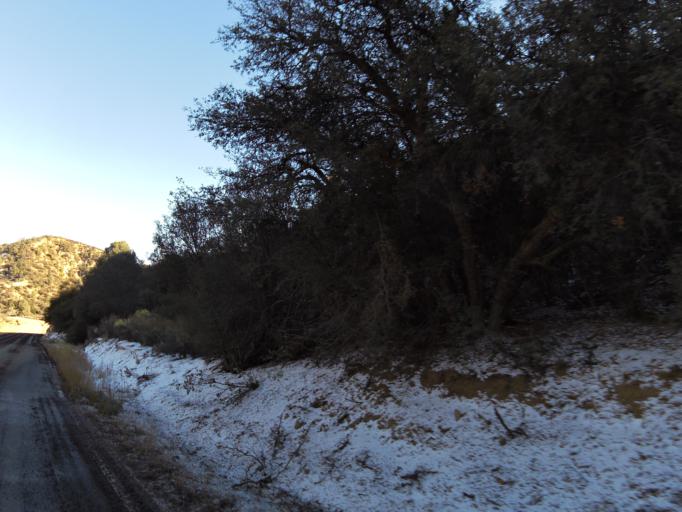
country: US
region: California
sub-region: Ventura County
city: Meiners Oaks
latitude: 34.6784
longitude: -119.3642
